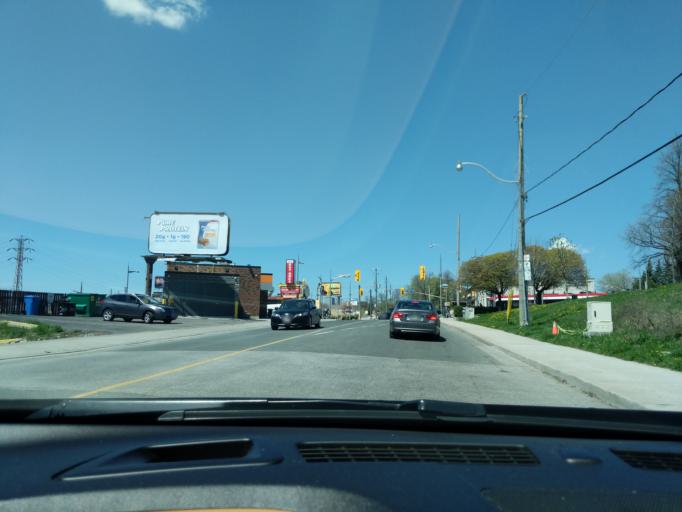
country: CA
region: Ontario
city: Toronto
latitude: 43.6747
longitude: -79.4544
